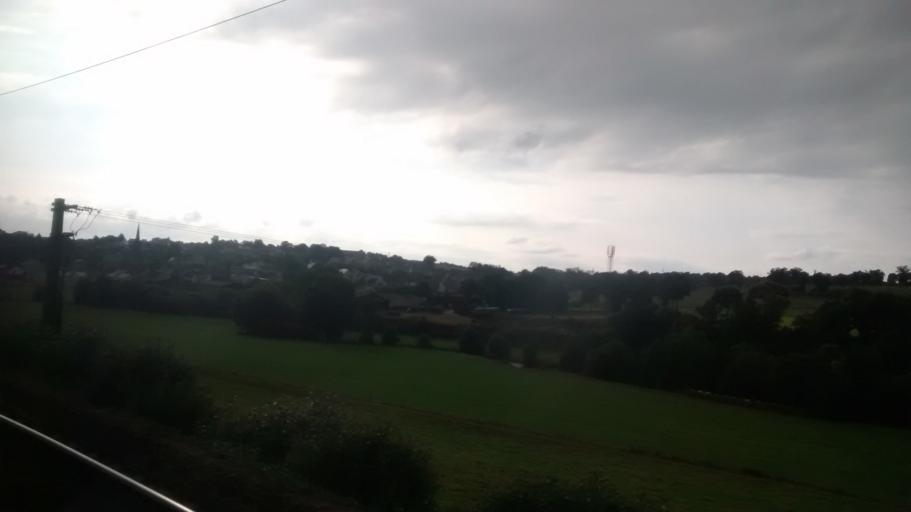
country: FR
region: Brittany
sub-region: Departement d'Ille-et-Vilaine
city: Poce-les-Bois
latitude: 48.1139
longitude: -1.2389
